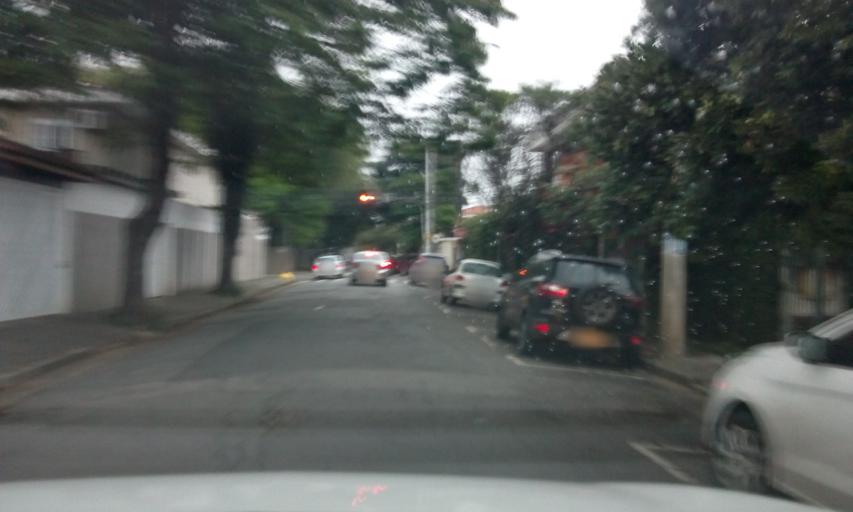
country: BR
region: Sao Paulo
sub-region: Sao Paulo
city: Sao Paulo
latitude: -23.6036
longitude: -46.6906
